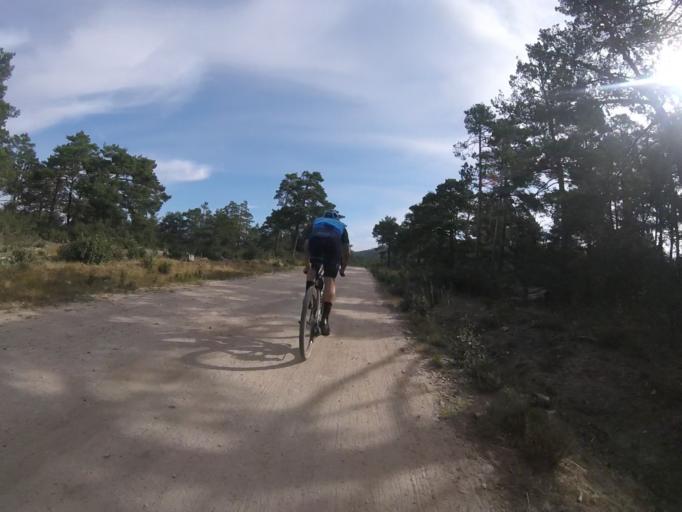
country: ES
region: Castille and Leon
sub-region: Provincia de Avila
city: Peguerinos
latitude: 40.6442
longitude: -4.1790
